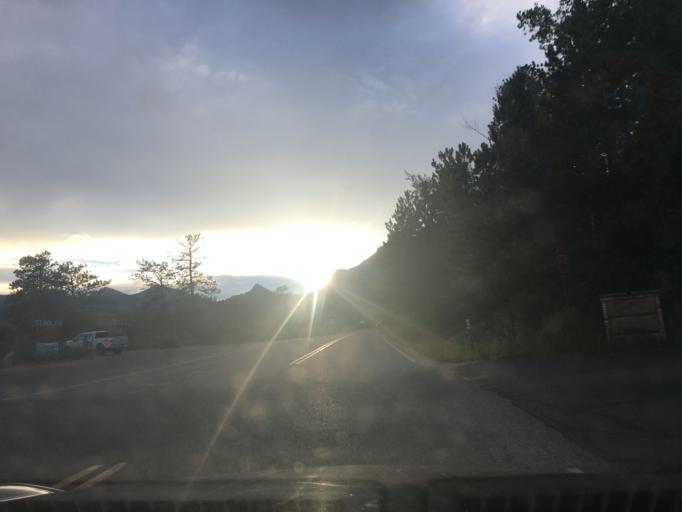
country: US
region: Colorado
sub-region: Larimer County
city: Estes Park
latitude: 40.4027
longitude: -105.5873
